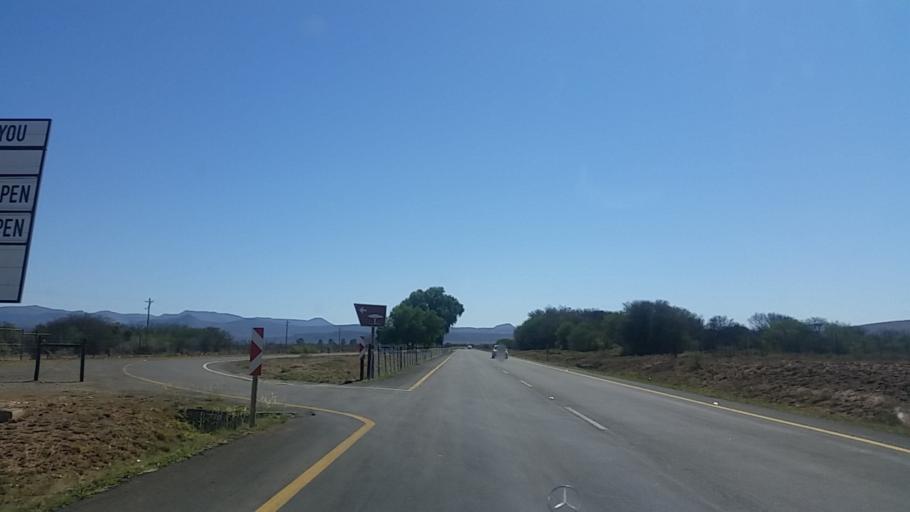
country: ZA
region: Eastern Cape
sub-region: Cacadu District Municipality
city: Graaff-Reinet
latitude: -32.2109
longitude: 24.5472
